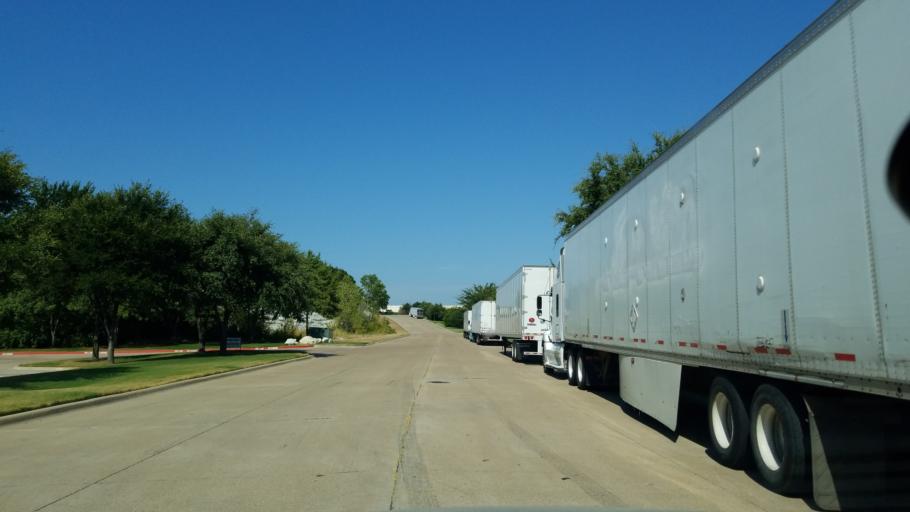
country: US
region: Texas
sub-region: Dallas County
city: Cockrell Hill
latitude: 32.7522
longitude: -96.8875
